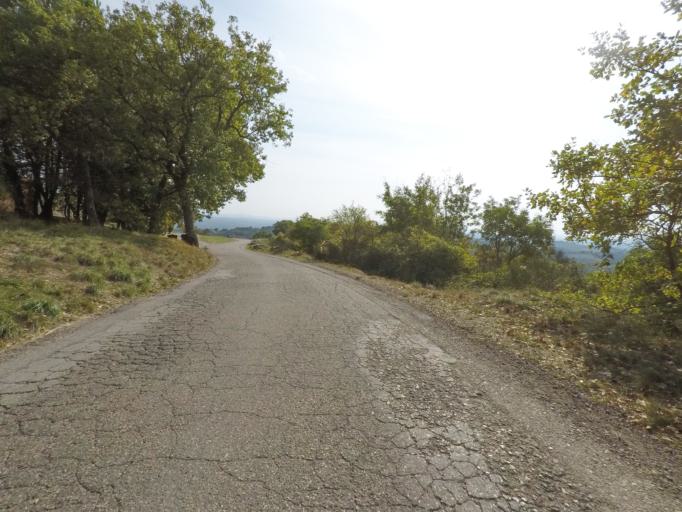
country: IT
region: Tuscany
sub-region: Provincia di Siena
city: Castellina in Chianti
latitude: 43.4186
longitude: 11.3431
